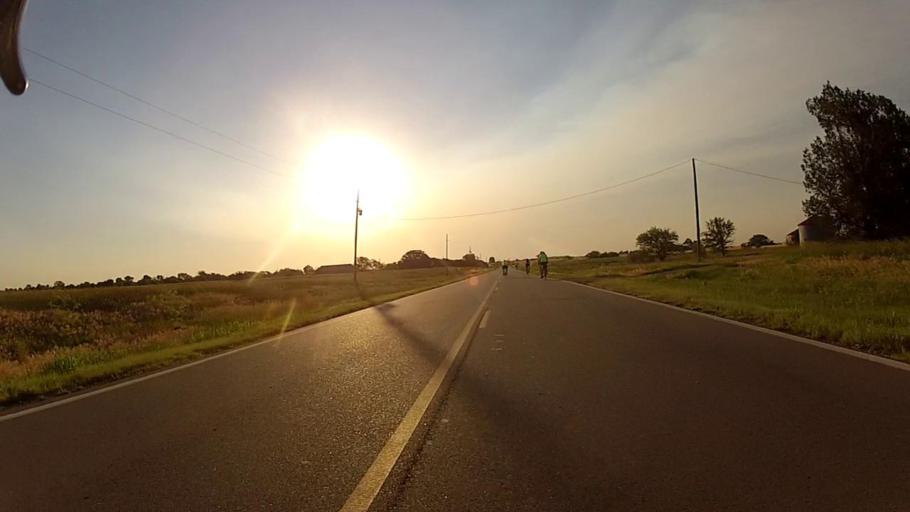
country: US
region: Kansas
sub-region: Harper County
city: Anthony
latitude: 37.1534
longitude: -97.8873
